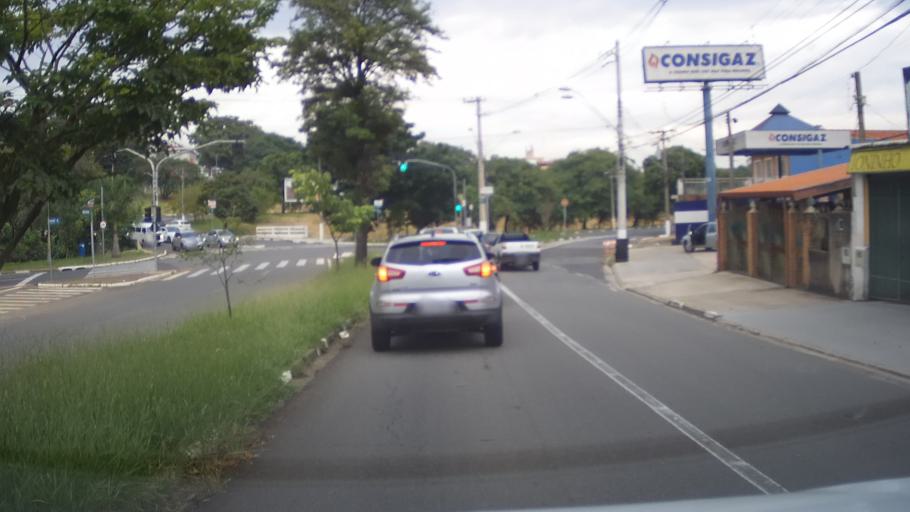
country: BR
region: Sao Paulo
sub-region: Campinas
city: Campinas
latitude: -22.9272
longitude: -47.0606
